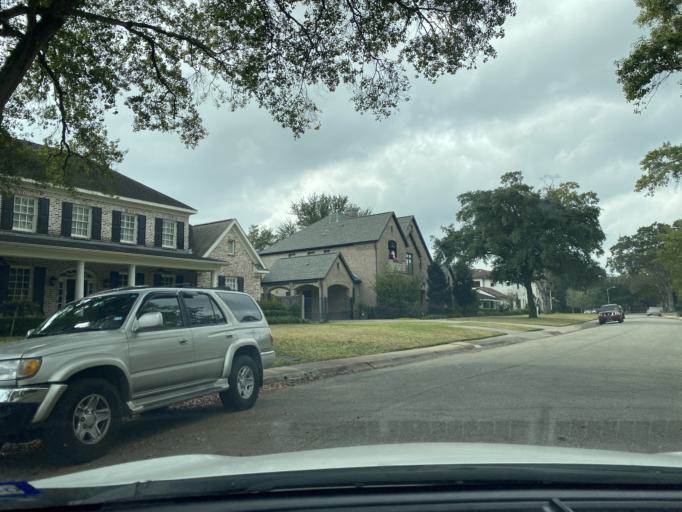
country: US
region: Texas
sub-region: Harris County
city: Hunters Creek Village
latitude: 29.7480
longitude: -95.4751
